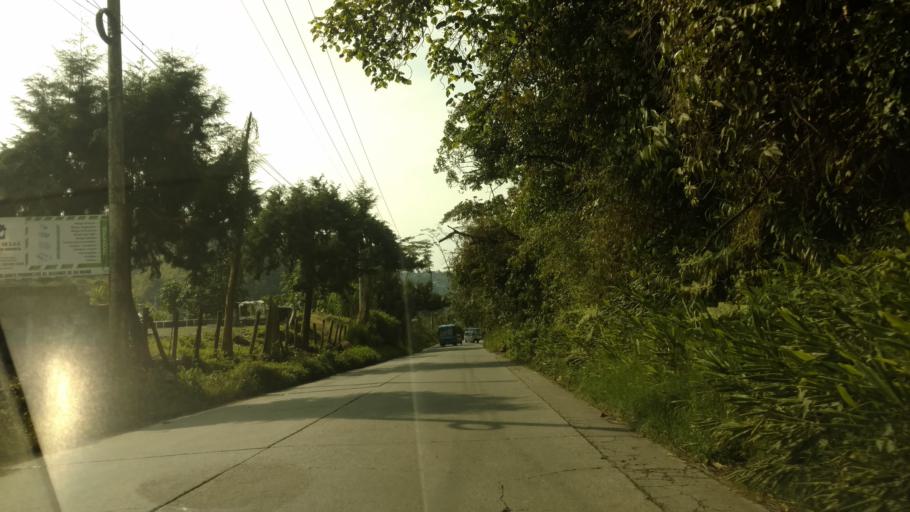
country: CO
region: Caldas
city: Manizales
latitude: 5.0762
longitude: -75.5095
